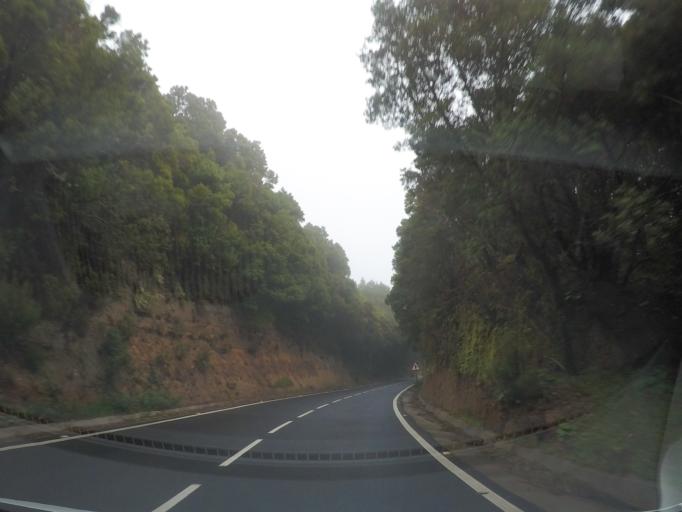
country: ES
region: Canary Islands
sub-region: Provincia de Santa Cruz de Tenerife
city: Vallehermosa
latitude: 28.1267
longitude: -17.2601
